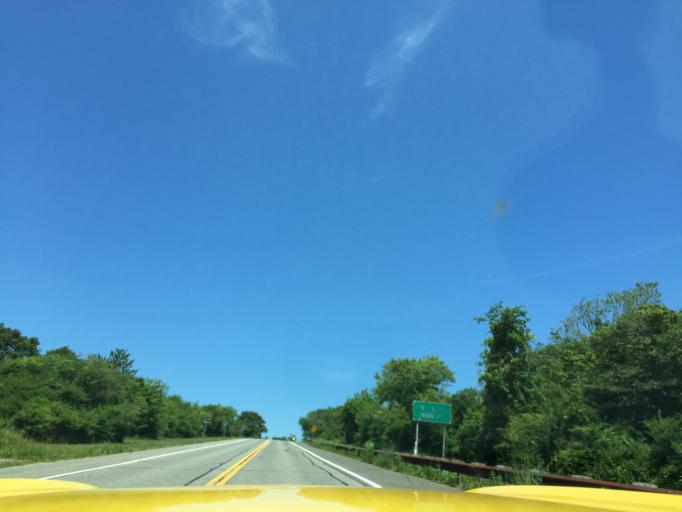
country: US
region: New York
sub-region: Suffolk County
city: Montauk
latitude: 41.0561
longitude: -71.8970
